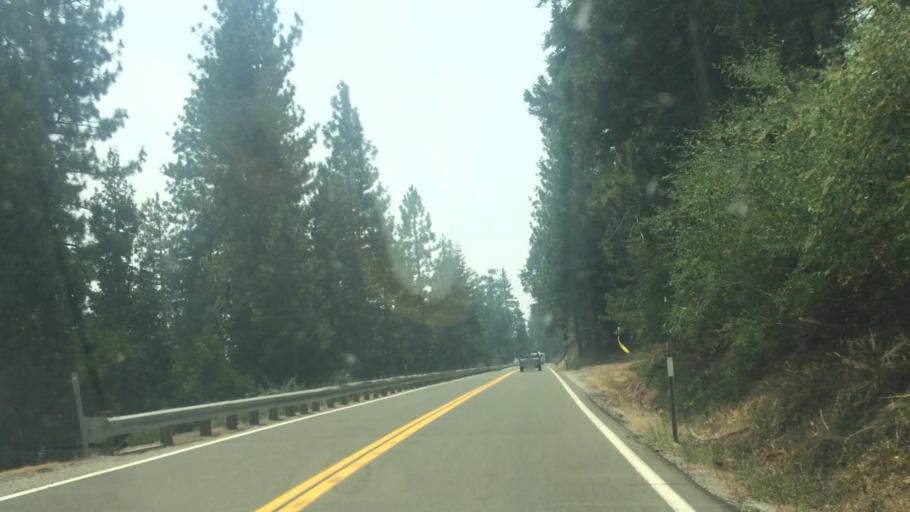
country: US
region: California
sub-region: Amador County
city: Pioneer
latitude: 38.5406
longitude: -120.3819
